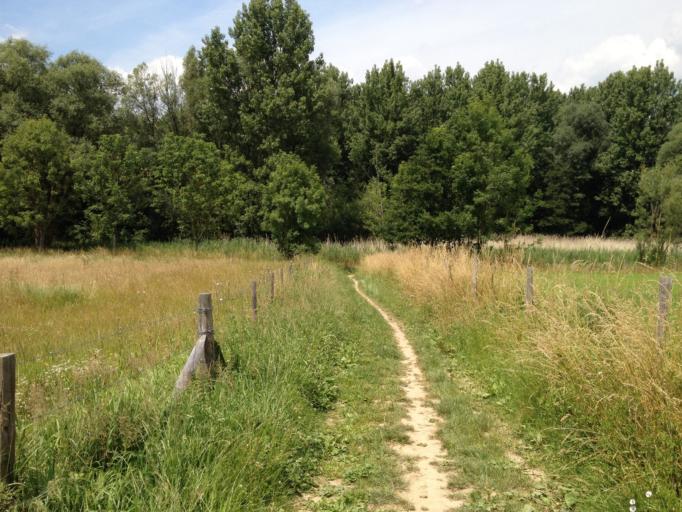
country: BE
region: Flanders
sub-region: Provincie Vlaams-Brabant
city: Bever
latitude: 50.9107
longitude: 4.3169
